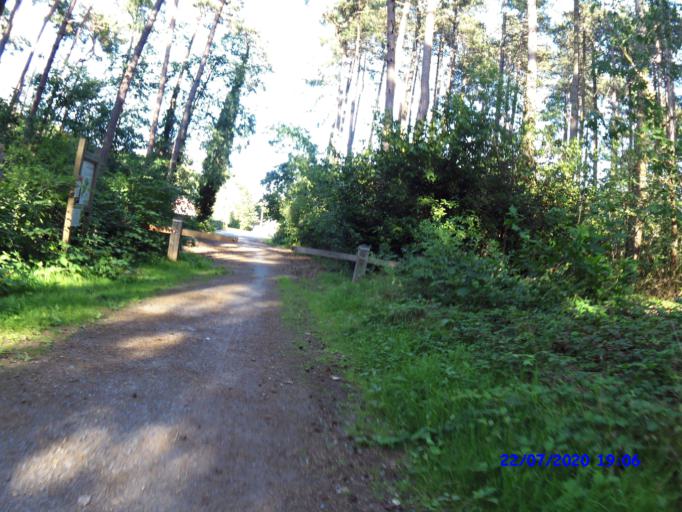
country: BE
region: Flanders
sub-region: Provincie Vlaams-Brabant
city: Aarschot
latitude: 50.9965
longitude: 4.8205
